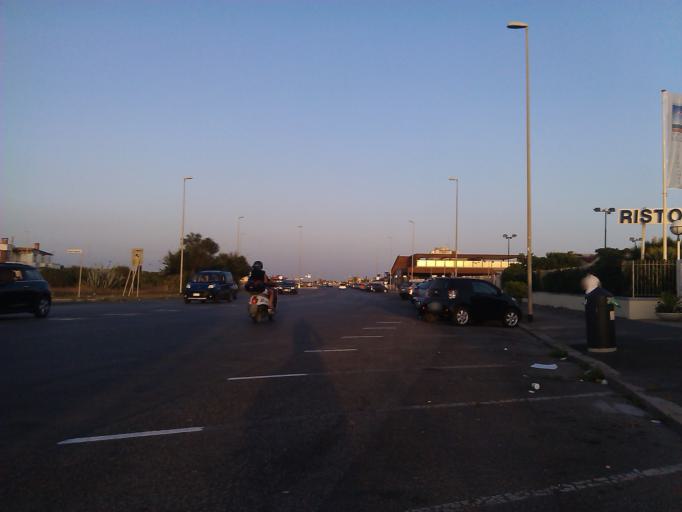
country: IT
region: Latium
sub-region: Citta metropolitana di Roma Capitale
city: Lido di Ostia
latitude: 41.7141
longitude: 12.3180
